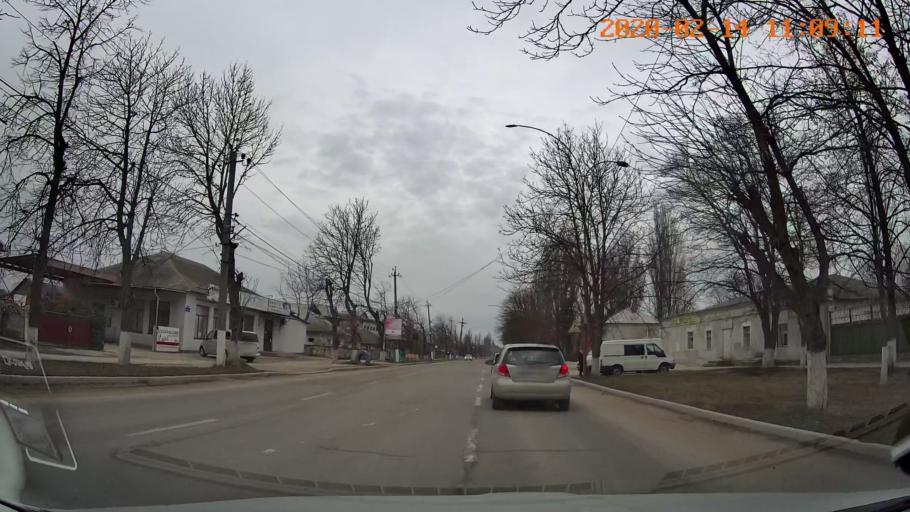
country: MD
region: Raionul Edinet
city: Edinet
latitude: 48.1765
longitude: 27.2960
